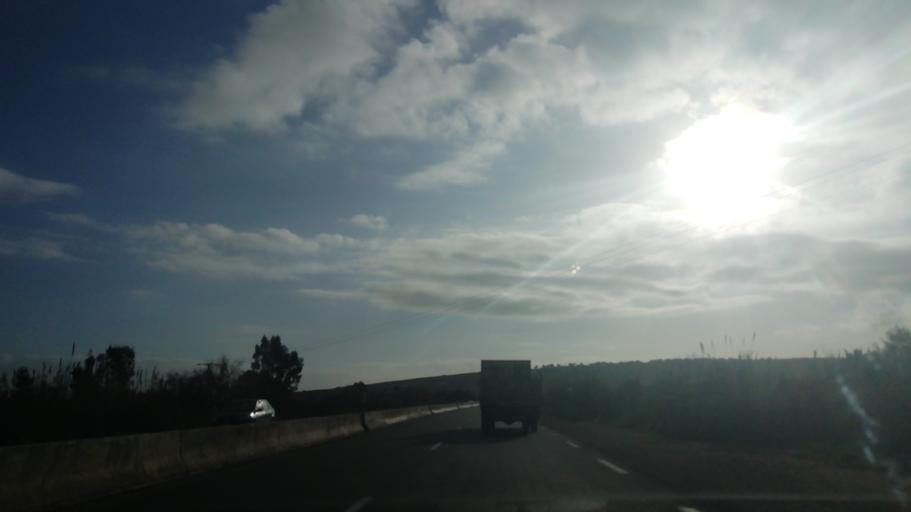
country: DZ
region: Mostaganem
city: Mostaganem
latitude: 36.0984
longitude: 0.2703
